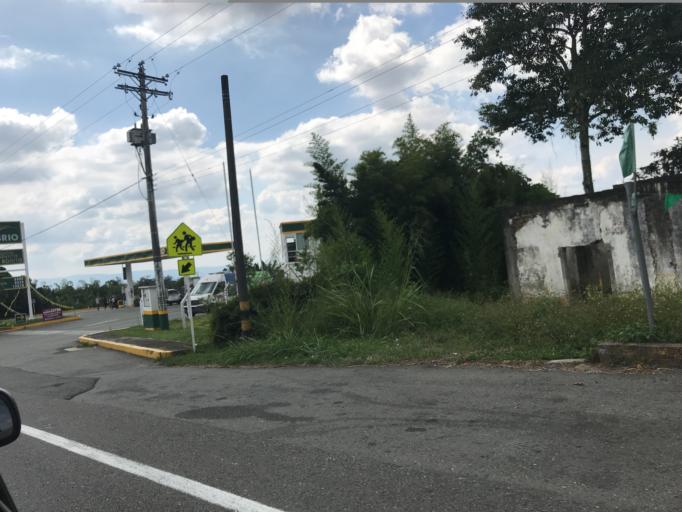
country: CO
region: Quindio
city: Armenia
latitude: 4.4879
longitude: -75.6954
